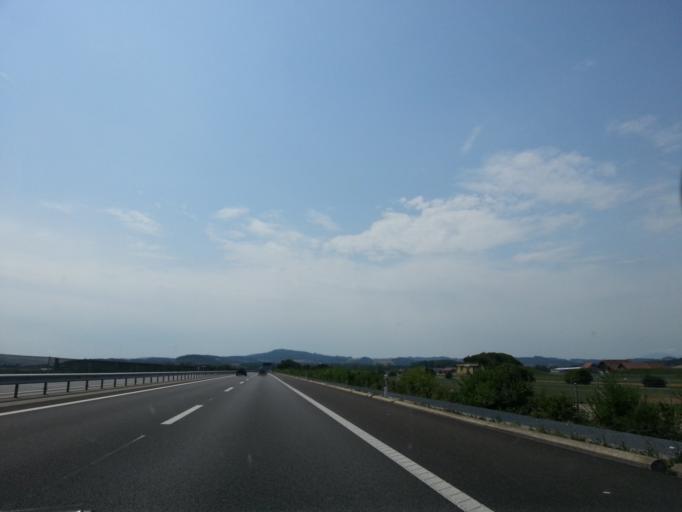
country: CH
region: Vaud
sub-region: Broye-Vully District
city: Payerne
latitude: 46.8444
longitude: 6.9314
